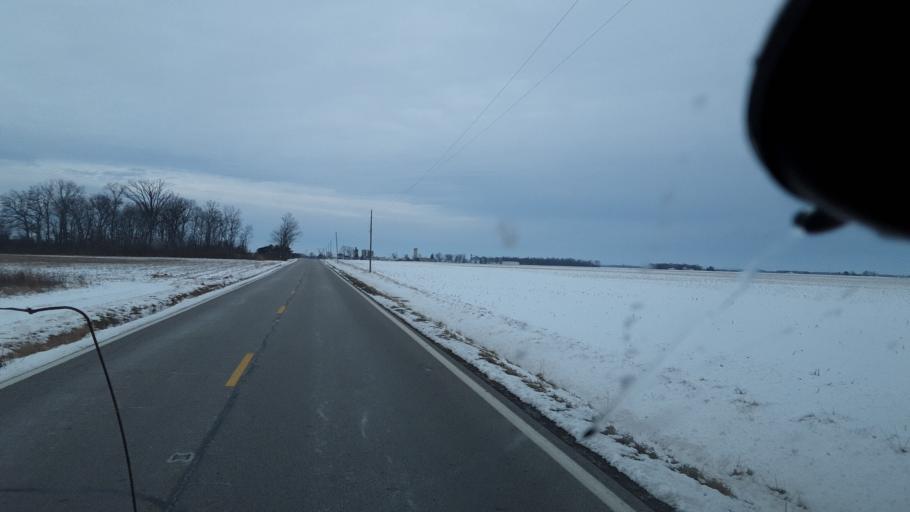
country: US
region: Ohio
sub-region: Pickaway County
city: Williamsport
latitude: 39.6491
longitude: -83.1076
